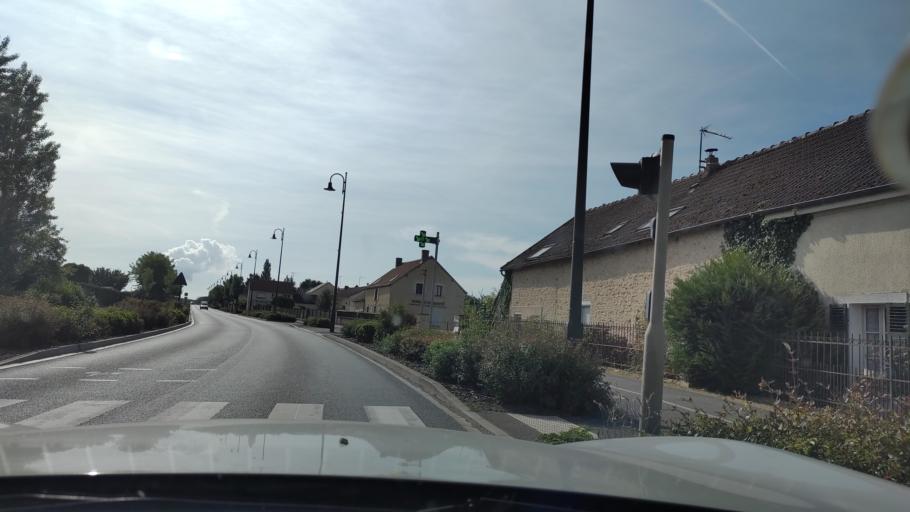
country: FR
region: Ile-de-France
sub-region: Departement de Seine-et-Marne
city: Sourdun
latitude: 48.5365
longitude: 3.3551
